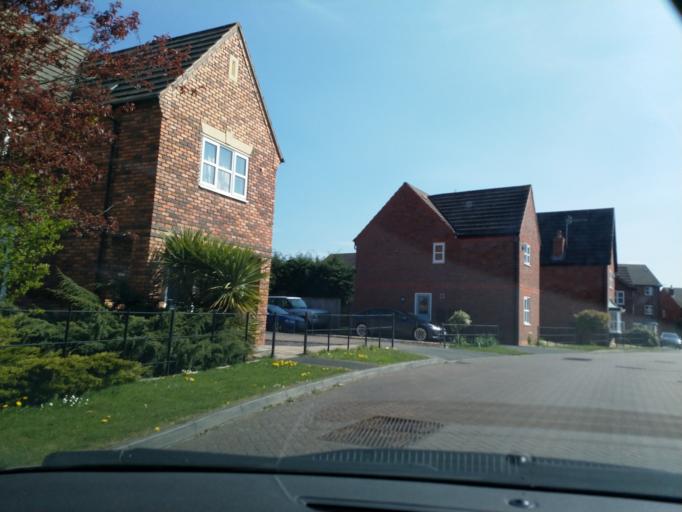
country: GB
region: England
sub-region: Warwickshire
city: Stratford-upon-Avon
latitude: 52.1942
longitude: -1.7261
